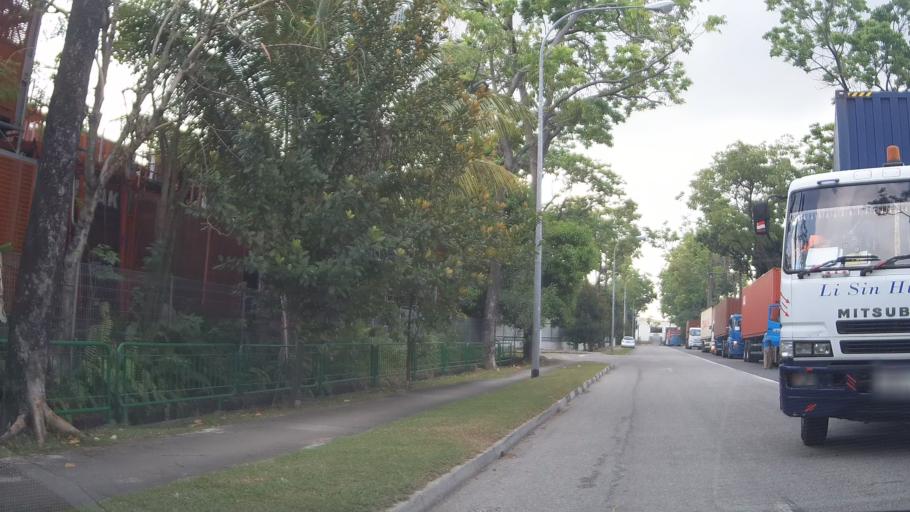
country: MY
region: Johor
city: Johor Bahru
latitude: 1.3186
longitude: 103.6446
